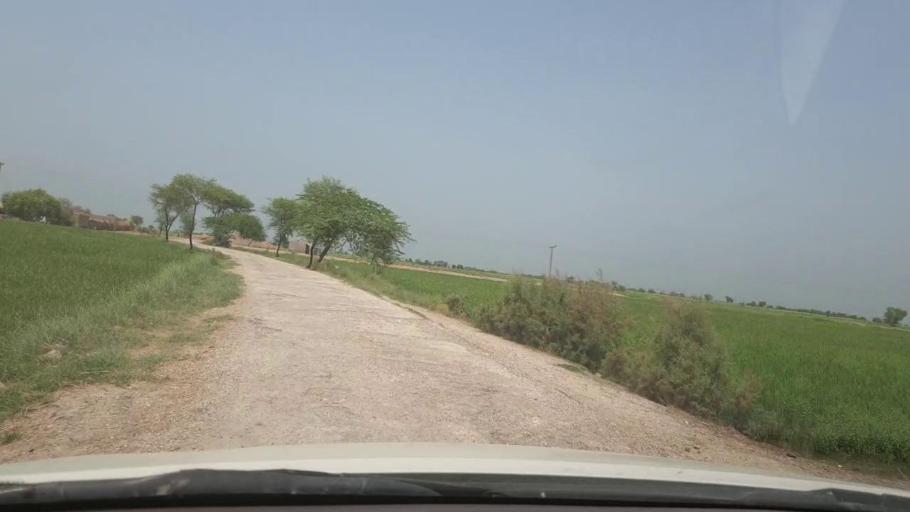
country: PK
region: Sindh
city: Shikarpur
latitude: 28.0711
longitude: 68.5754
